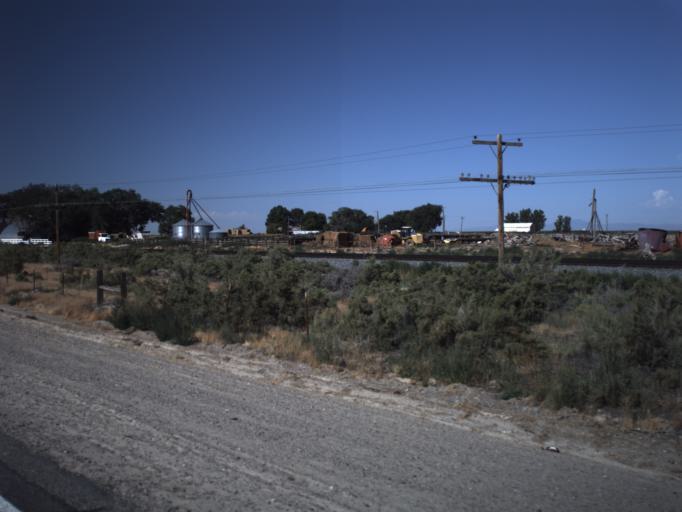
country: US
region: Utah
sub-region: Millard County
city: Delta
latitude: 39.5410
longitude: -112.3628
